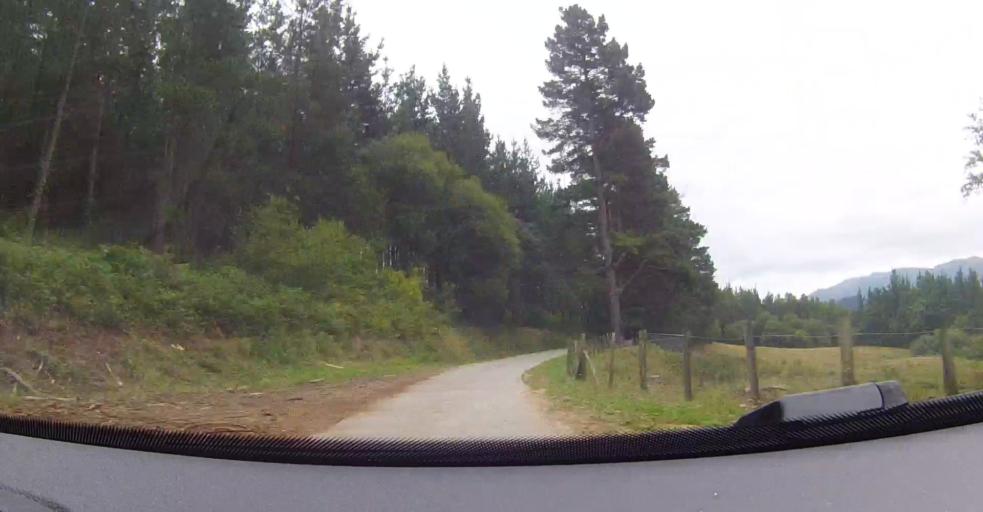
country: ES
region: Basque Country
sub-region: Bizkaia
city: Urrestieta
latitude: 43.2318
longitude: -3.1785
